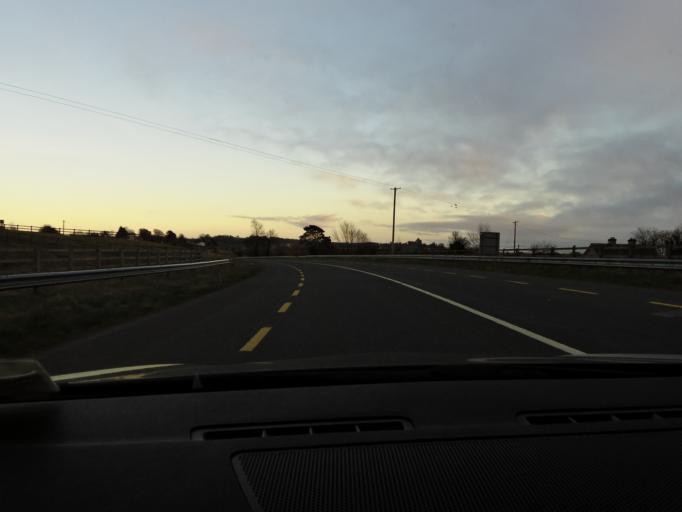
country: IE
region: Connaught
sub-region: Sligo
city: Ballymote
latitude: 53.9802
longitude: -8.4636
